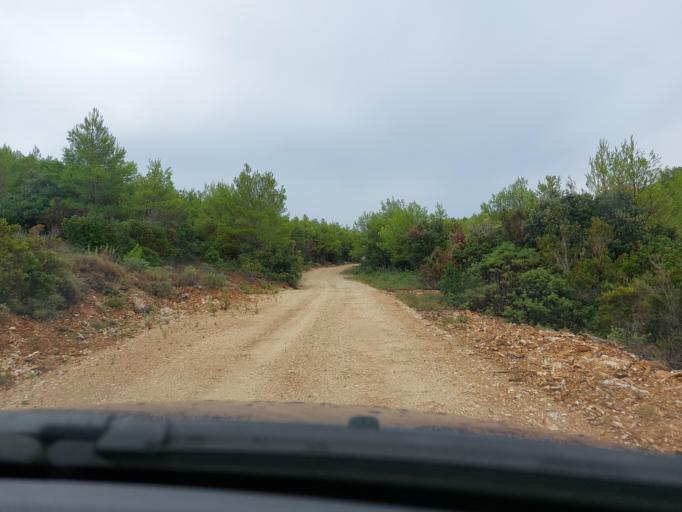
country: HR
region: Dubrovacko-Neretvanska
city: Smokvica
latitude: 42.7463
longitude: 16.9164
